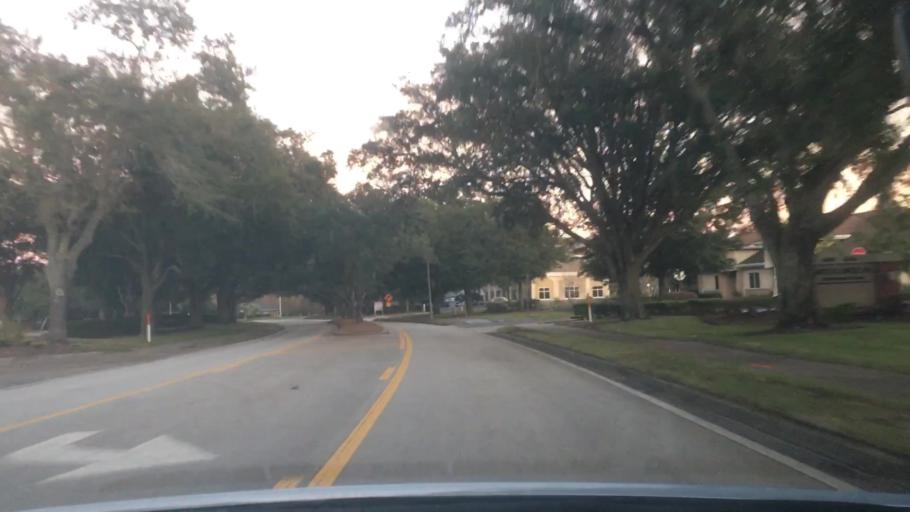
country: US
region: Florida
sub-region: Duval County
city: Jacksonville
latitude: 30.2582
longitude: -81.5903
